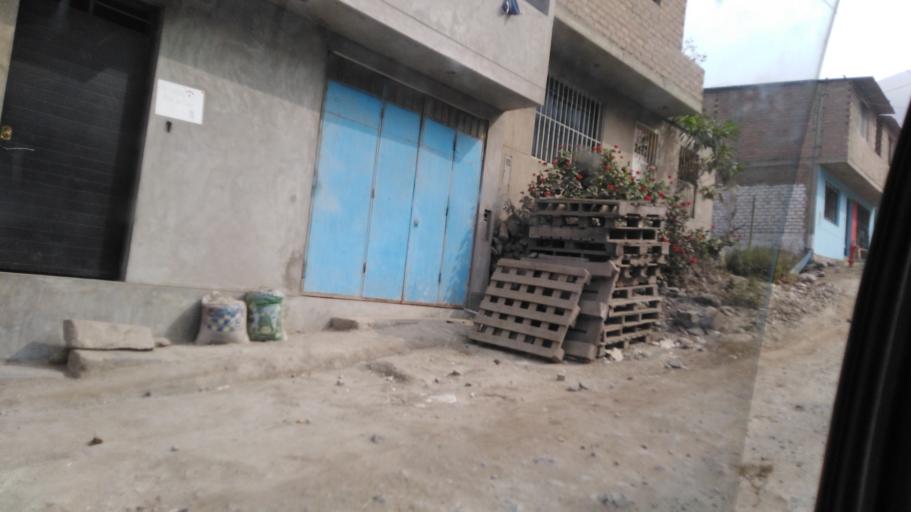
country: PE
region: Lima
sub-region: Lima
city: La Molina
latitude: -12.1454
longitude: -76.9261
